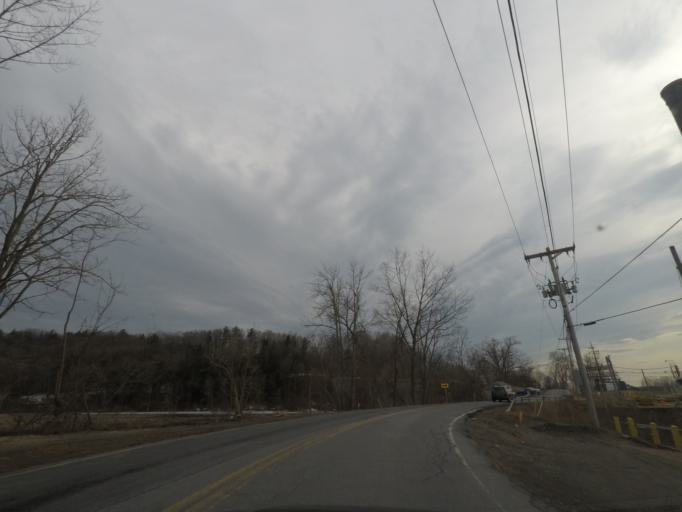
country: US
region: New York
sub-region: Saratoga County
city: Schuylerville
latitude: 43.1152
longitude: -73.5680
